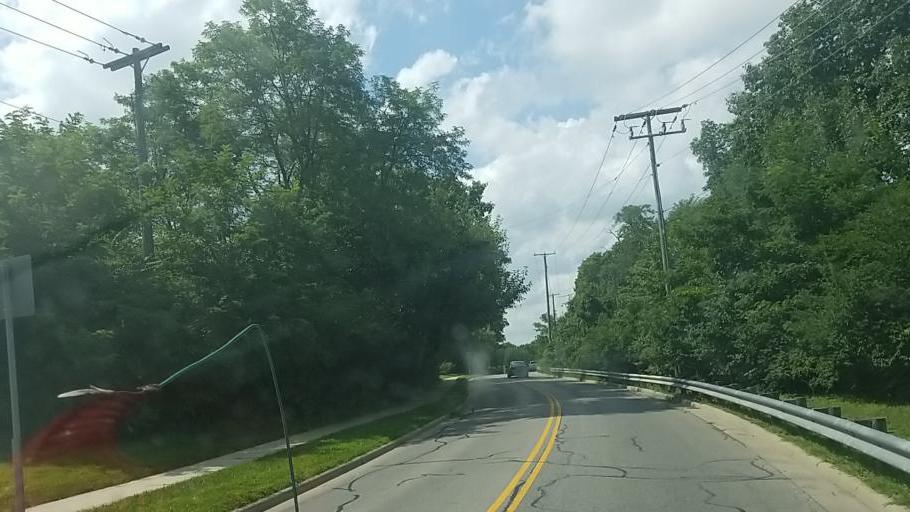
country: US
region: Ohio
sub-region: Franklin County
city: Gahanna
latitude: 40.0453
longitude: -82.8885
